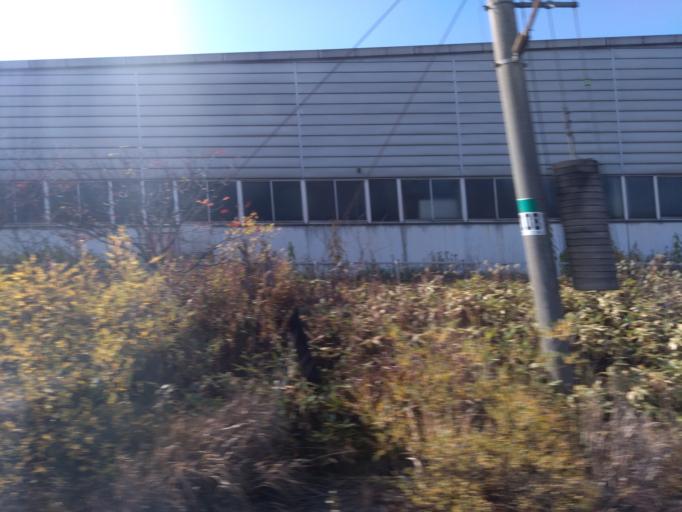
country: JP
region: Hokkaido
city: Kitahiroshima
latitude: 42.9265
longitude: 141.5729
